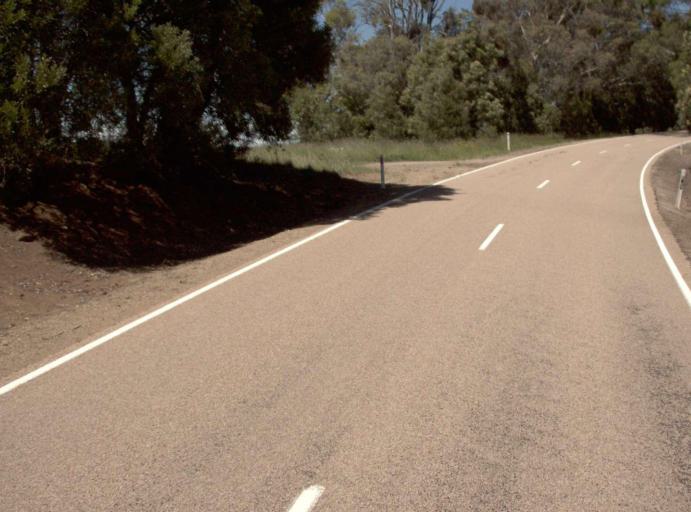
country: AU
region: Victoria
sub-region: East Gippsland
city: Lakes Entrance
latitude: -37.2473
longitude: 148.2551
